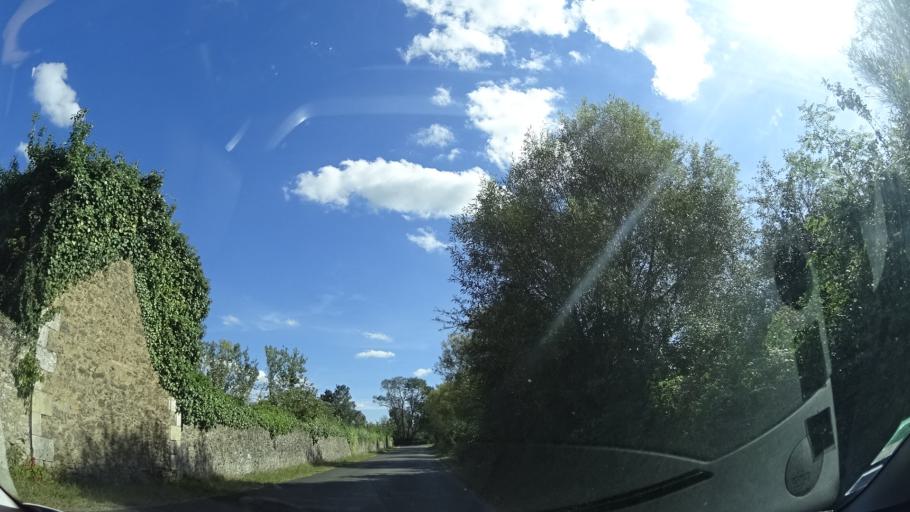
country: FR
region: Pays de la Loire
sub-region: Departement de la Sarthe
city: La Fleche
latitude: 47.6944
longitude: -0.0799
